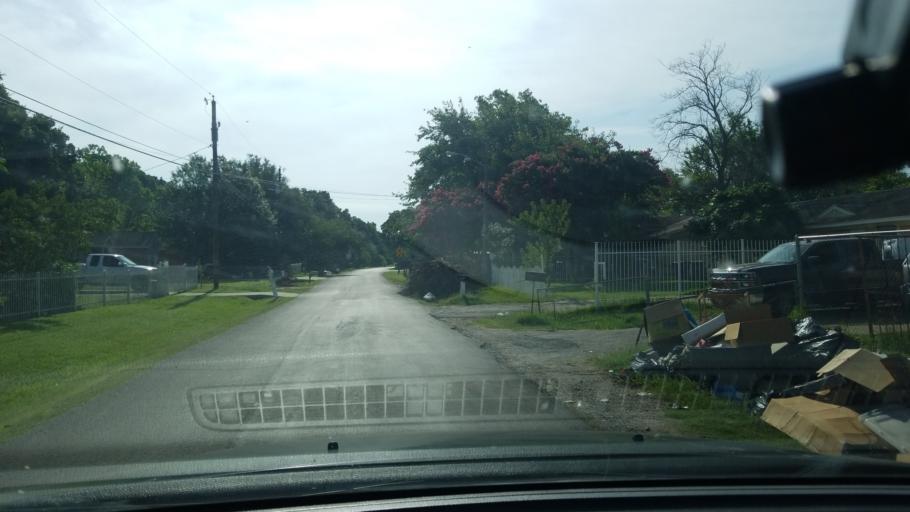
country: US
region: Texas
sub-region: Dallas County
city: Balch Springs
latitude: 32.7152
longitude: -96.6447
